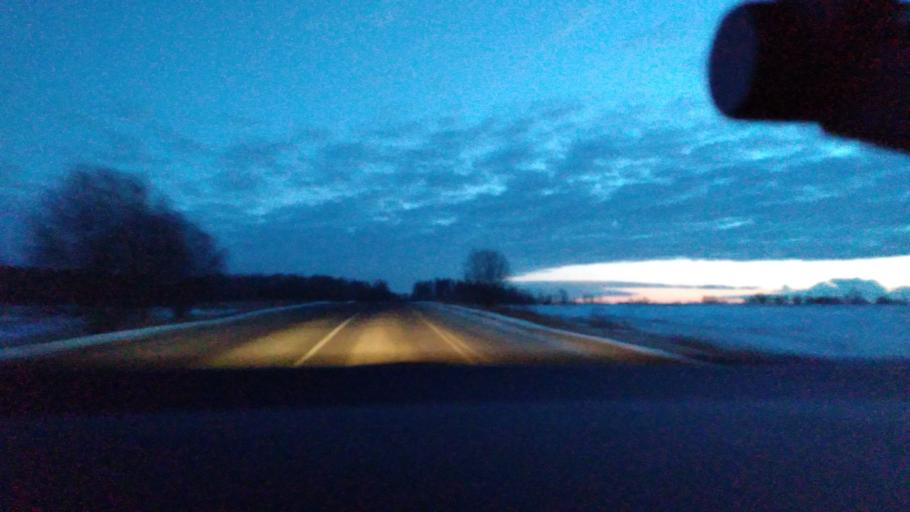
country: RU
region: Moskovskaya
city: Krasnaya Poyma
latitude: 55.1577
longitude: 39.2213
